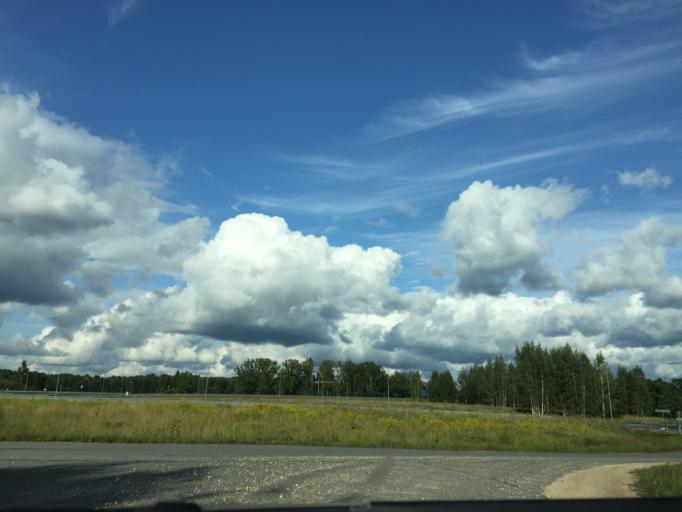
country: LV
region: Kegums
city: Kegums
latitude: 56.8227
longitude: 24.7570
